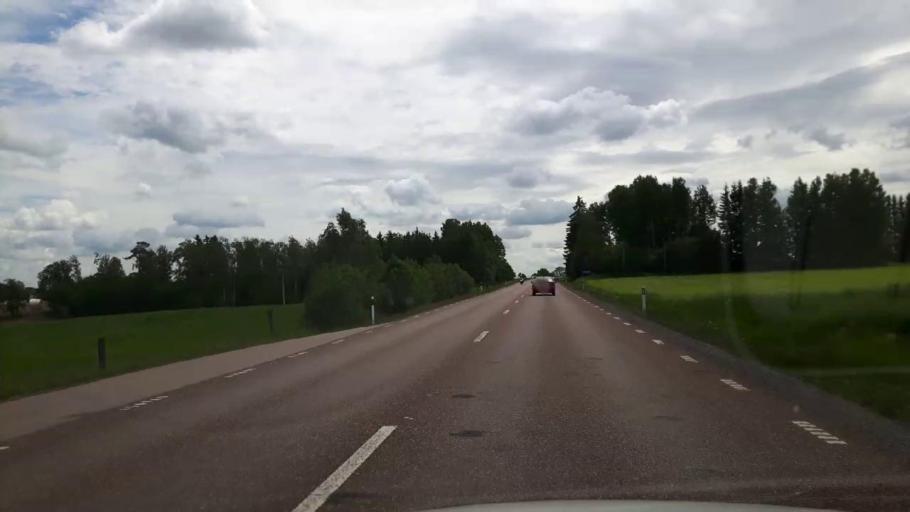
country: SE
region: Dalarna
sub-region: Hedemora Kommun
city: Hedemora
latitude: 60.3056
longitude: 15.9748
